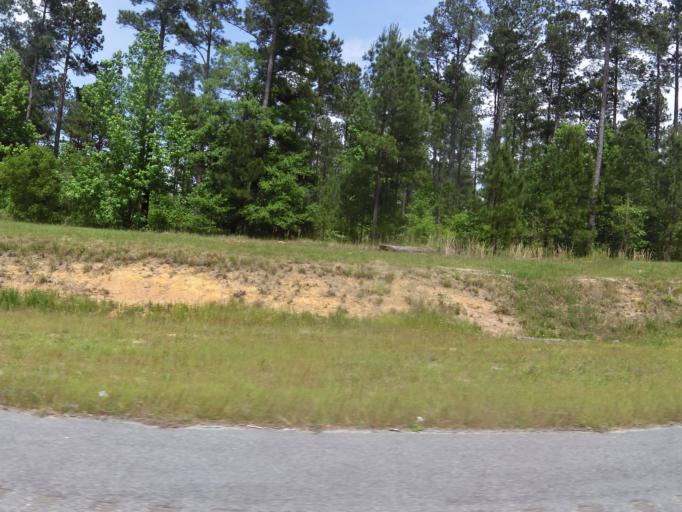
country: US
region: Georgia
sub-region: Jefferson County
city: Wadley
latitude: 32.7795
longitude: -82.3884
